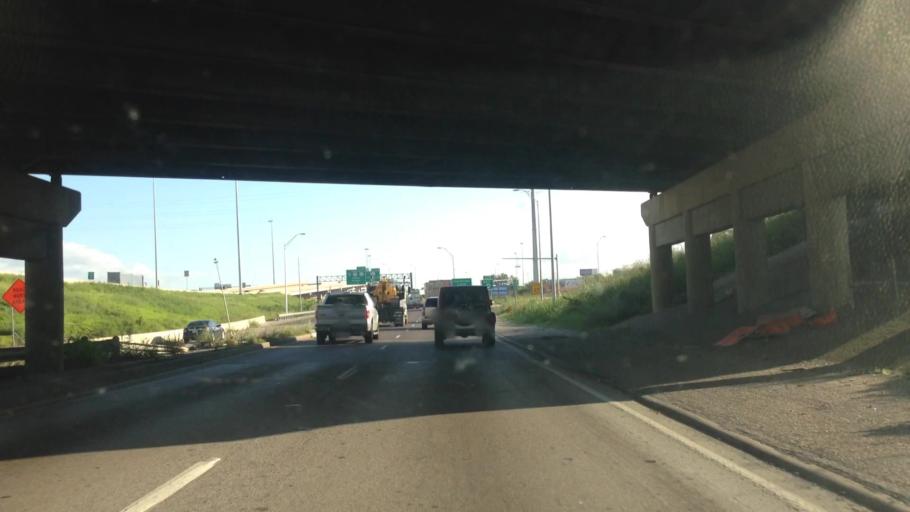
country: US
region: Texas
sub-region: Tarrant County
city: Fort Worth
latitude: 32.7642
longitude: -97.3188
